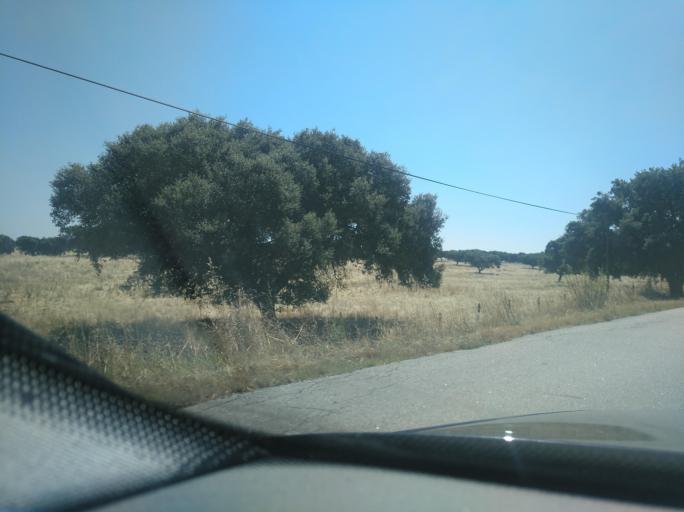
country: PT
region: Portalegre
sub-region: Arronches
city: Arronches
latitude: 38.9955
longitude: -7.3471
